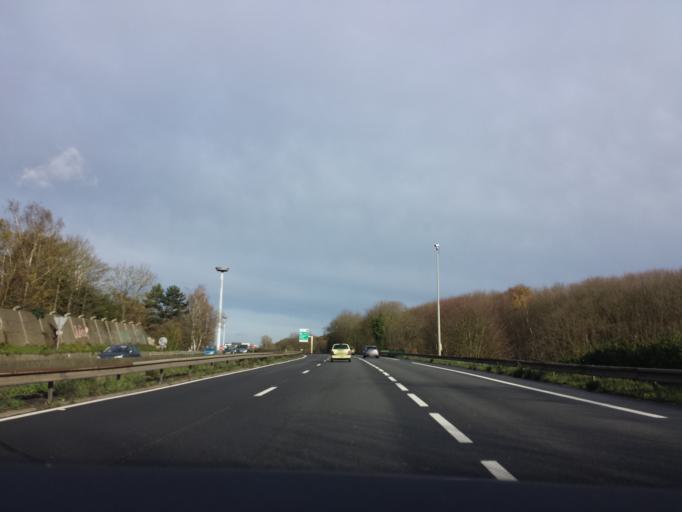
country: FR
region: Ile-de-France
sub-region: Departement de l'Essonne
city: Bievres
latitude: 48.7656
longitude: 2.2299
